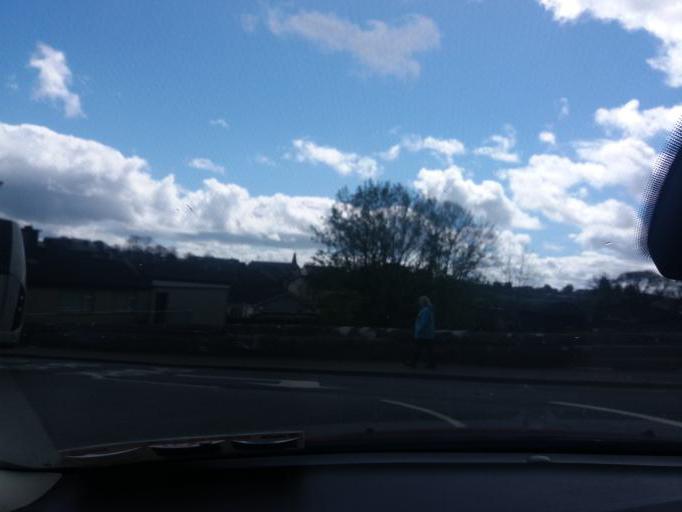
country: IE
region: Munster
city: Cashel
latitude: 52.5197
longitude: -7.8893
